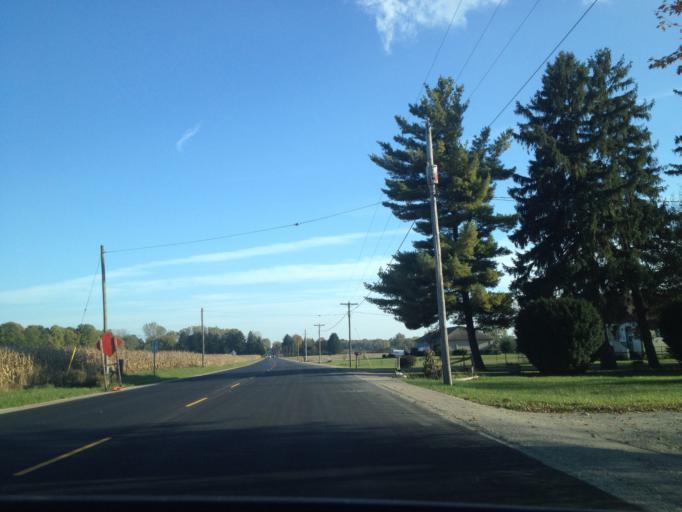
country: CA
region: Ontario
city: Delaware
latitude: 42.5866
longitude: -81.5856
